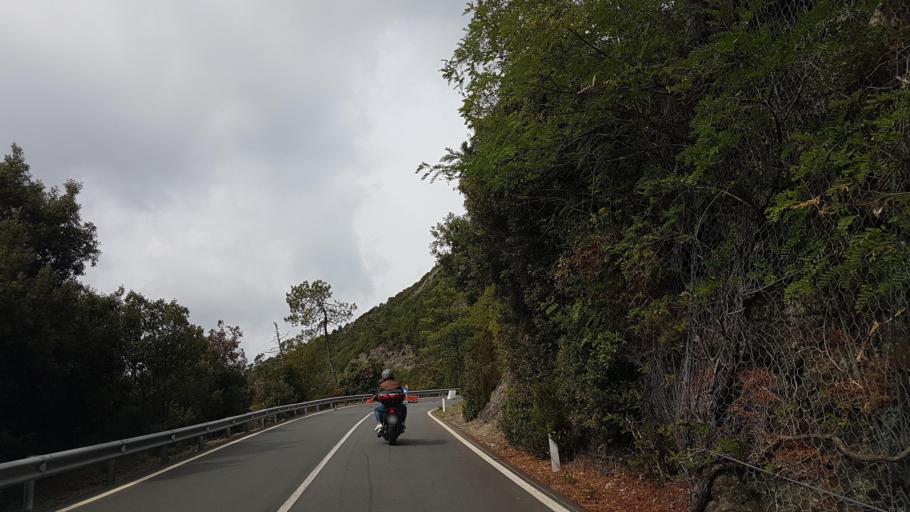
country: IT
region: Liguria
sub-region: Provincia di La Spezia
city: Framura
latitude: 44.2512
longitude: 9.5672
